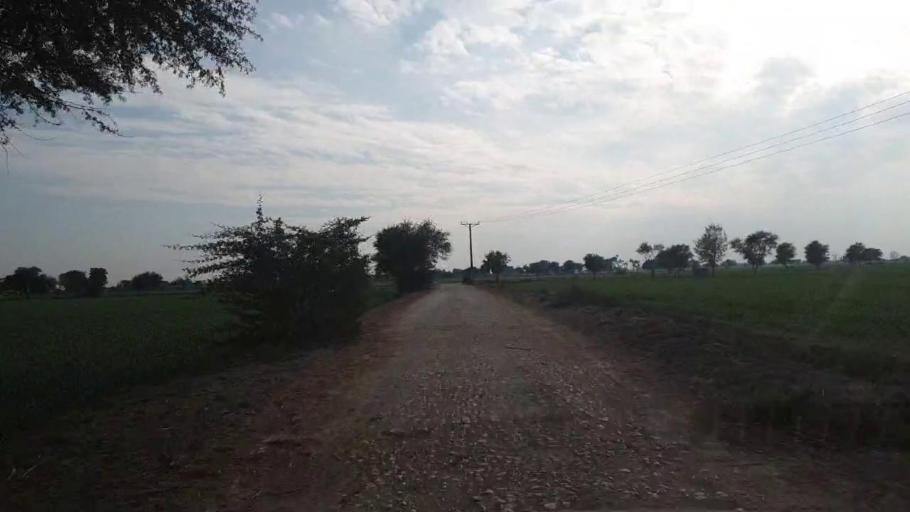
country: PK
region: Sindh
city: Shahpur Chakar
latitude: 26.0513
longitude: 68.5783
